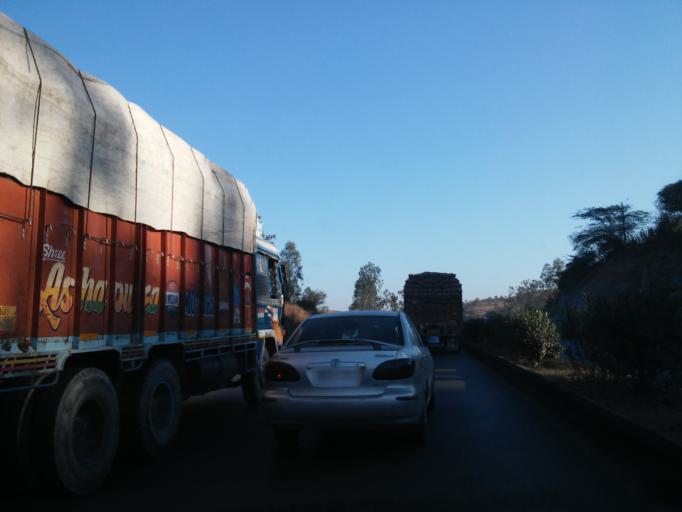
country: IN
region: Rajasthan
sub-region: Dungarpur
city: Dungarpur
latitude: 23.8931
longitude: 73.5418
